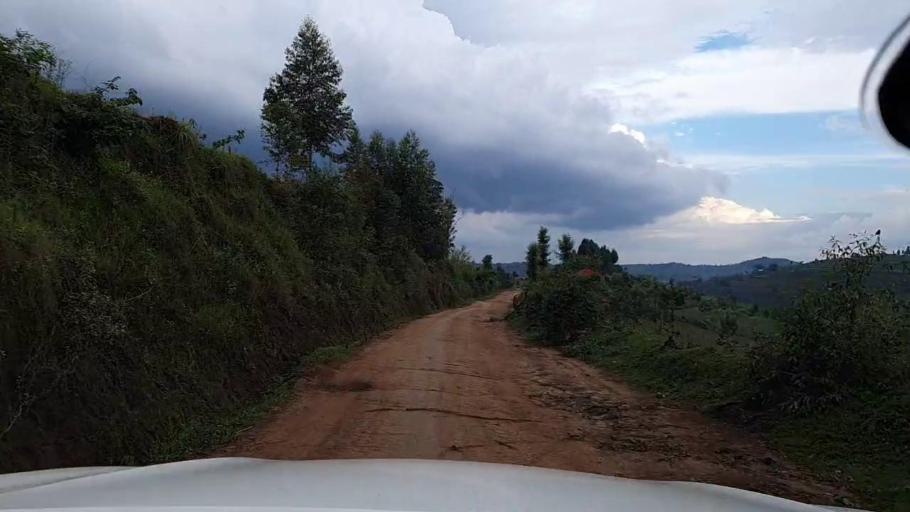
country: BI
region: Kayanza
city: Kayanza
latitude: -2.7953
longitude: 29.5147
